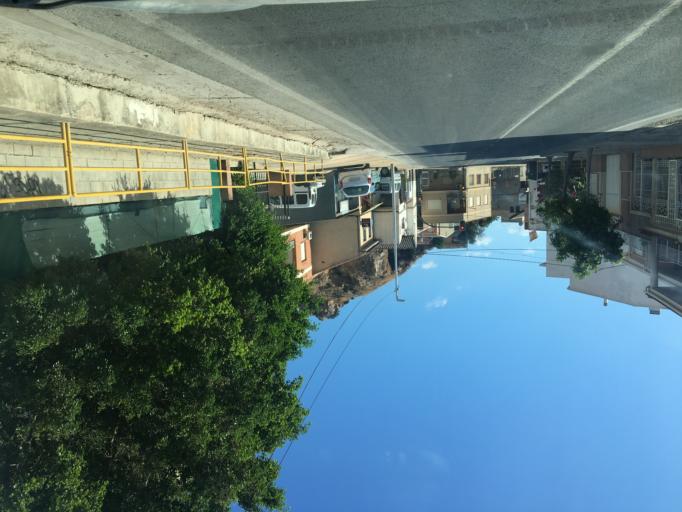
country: ES
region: Murcia
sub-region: Murcia
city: Murcia
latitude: 38.0222
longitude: -1.0877
